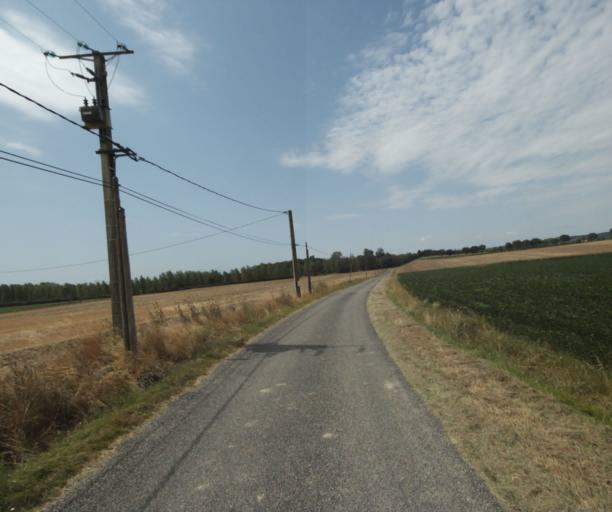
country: FR
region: Midi-Pyrenees
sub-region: Departement de la Haute-Garonne
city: Saint-Felix-Lauragais
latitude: 43.4277
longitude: 1.9187
